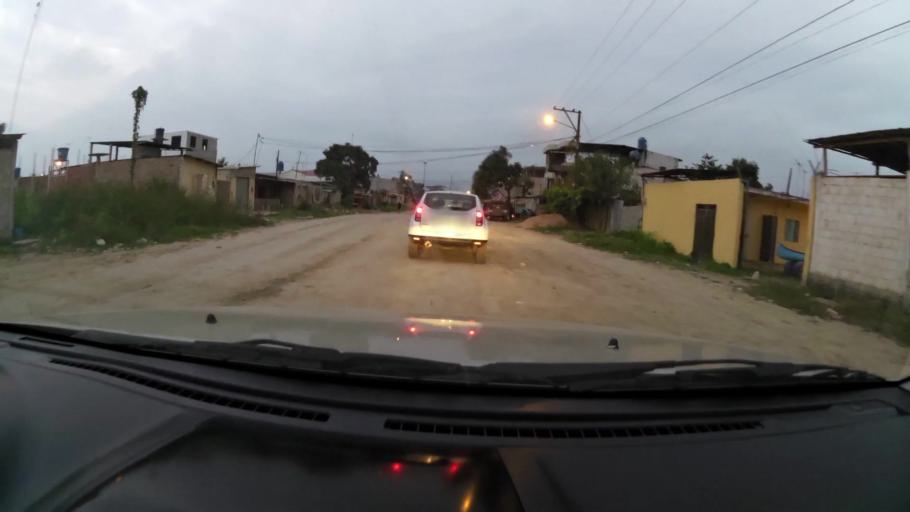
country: EC
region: El Oro
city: Machala
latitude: -3.2643
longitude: -79.9343
